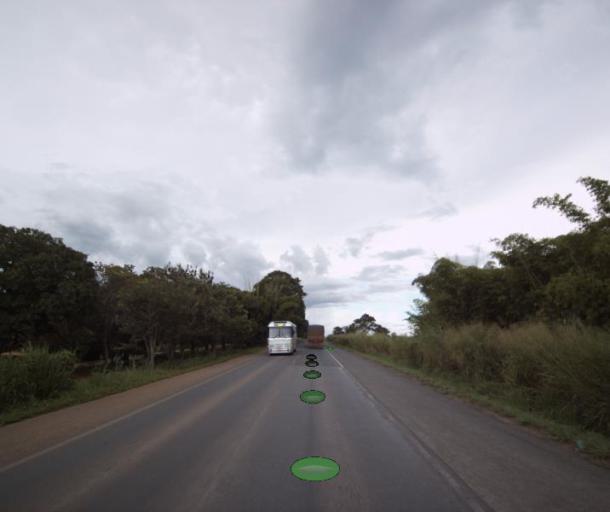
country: BR
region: Goias
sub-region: Itapaci
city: Itapaci
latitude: -15.0425
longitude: -49.4404
